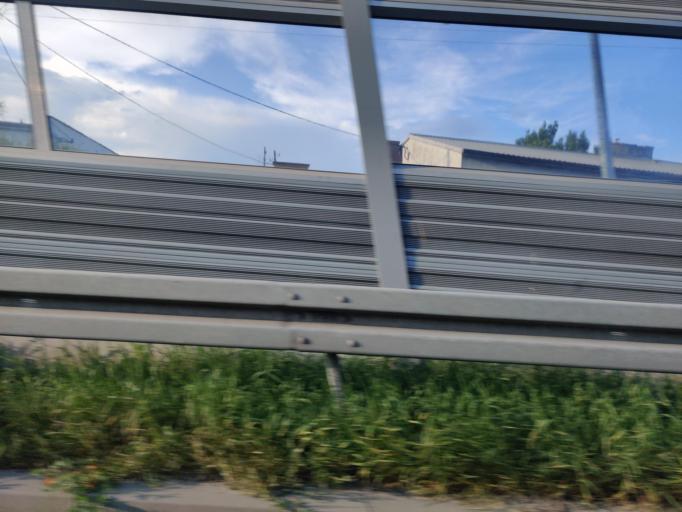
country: PL
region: Greater Poland Voivodeship
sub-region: Konin
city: Konin
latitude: 52.2023
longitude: 18.2760
